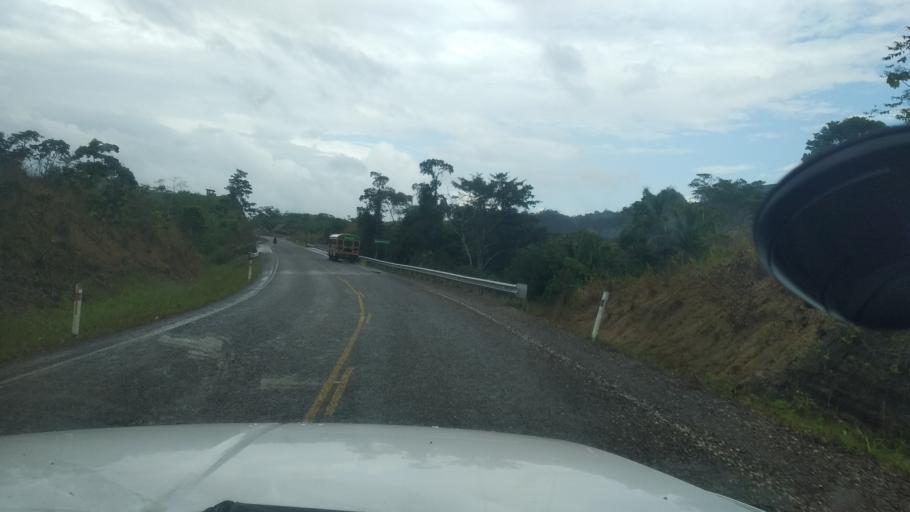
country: GT
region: Peten
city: San Luis
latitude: 16.1835
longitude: -89.1999
